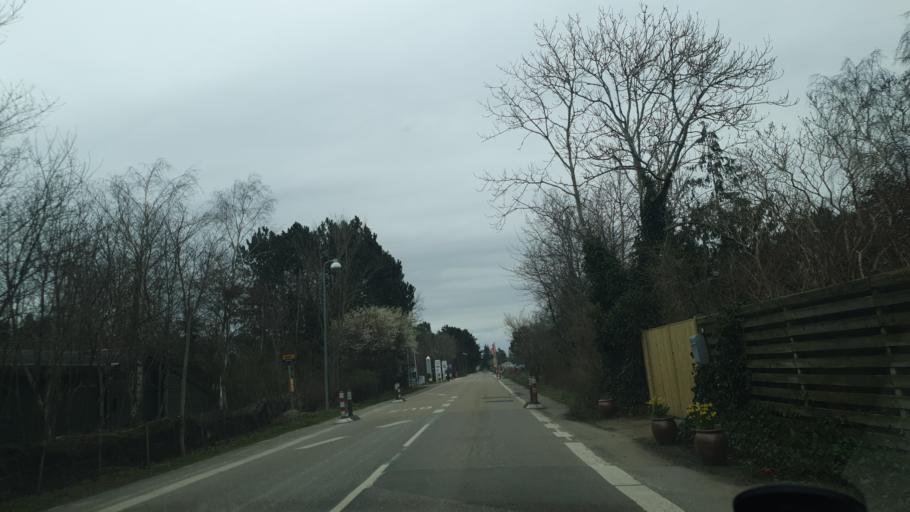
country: DK
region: Zealand
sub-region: Odsherred Kommune
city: Asnaes
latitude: 55.8570
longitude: 11.5245
